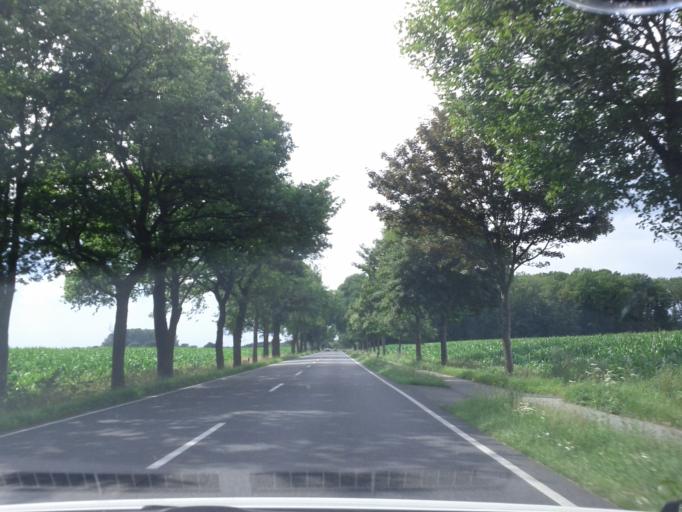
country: DE
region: Lower Saxony
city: Dudenbuttel
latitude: 53.5935
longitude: 9.3370
